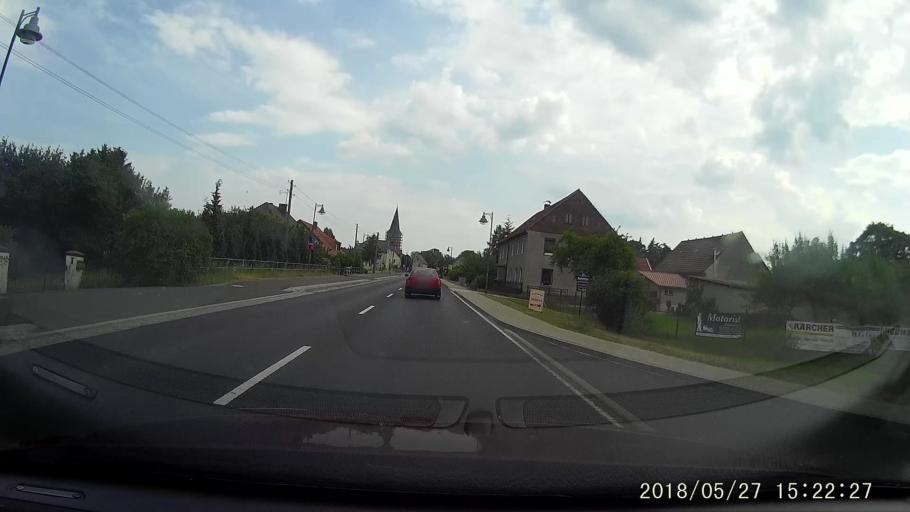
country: DE
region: Saxony
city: Kodersdorf
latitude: 51.2329
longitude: 14.8917
